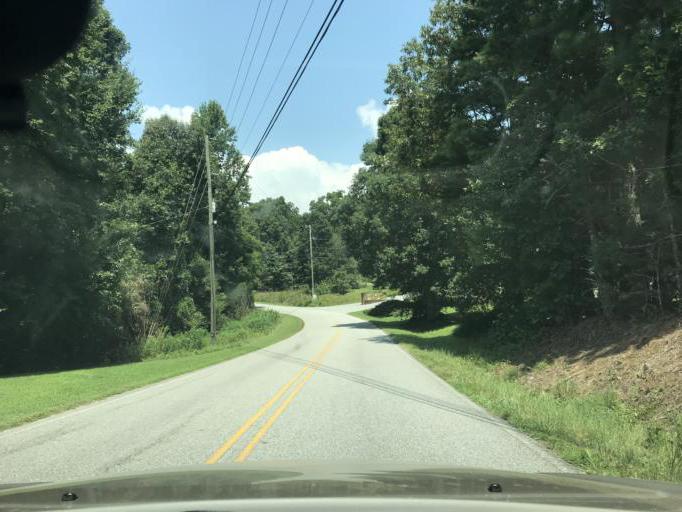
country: US
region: Georgia
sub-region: Dawson County
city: Dawsonville
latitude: 34.3447
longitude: -84.0832
